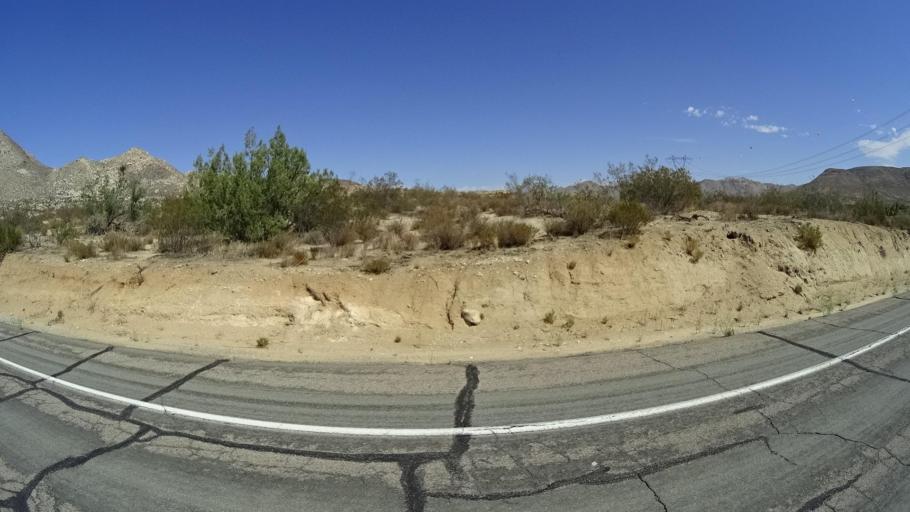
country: MX
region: Baja California
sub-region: Tecate
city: Cereso del Hongo
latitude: 32.6319
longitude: -116.1638
